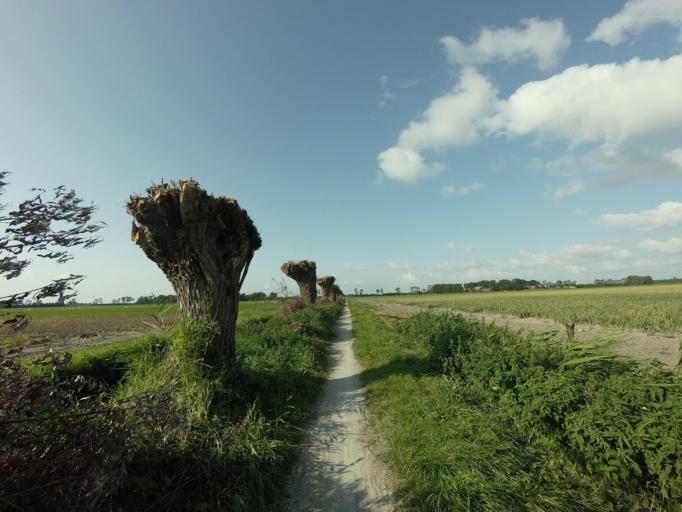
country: NL
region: Flevoland
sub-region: Gemeente Noordoostpolder
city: Emmeloord
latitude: 52.6623
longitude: 5.7752
